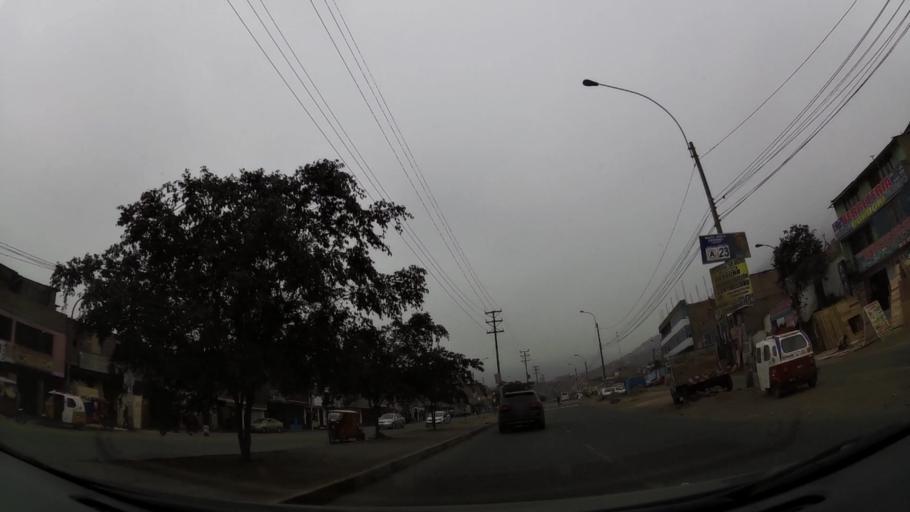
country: PE
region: Lima
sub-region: Lima
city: Urb. Santo Domingo
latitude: -11.8813
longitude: -77.0225
